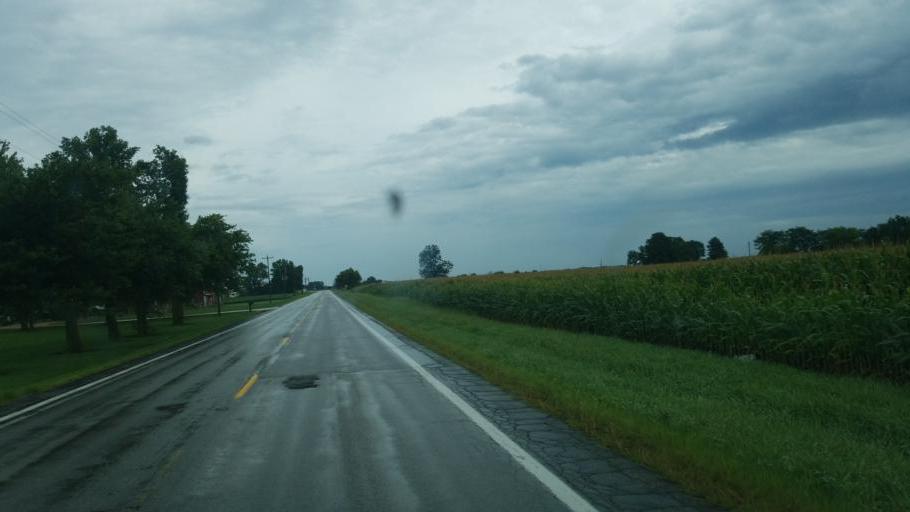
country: US
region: Ohio
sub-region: Delaware County
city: Delaware
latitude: 40.3254
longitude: -83.0142
